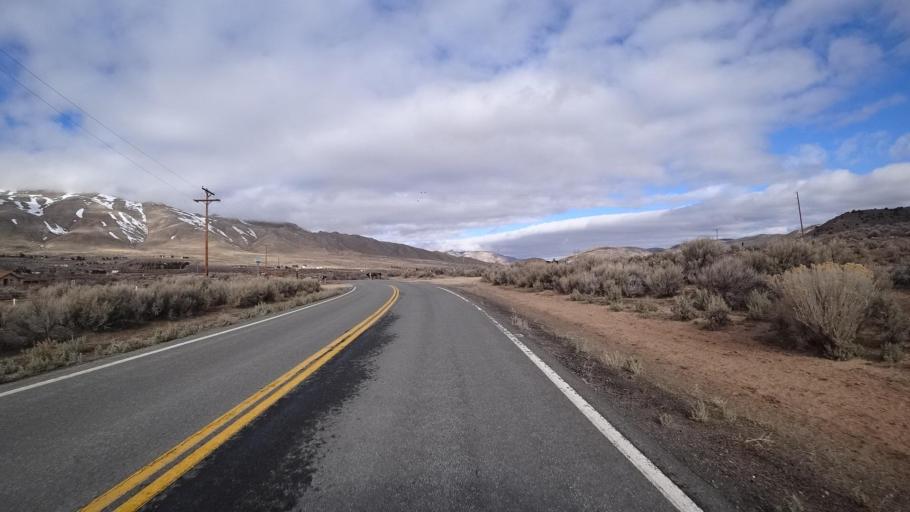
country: US
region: Nevada
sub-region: Washoe County
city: Cold Springs
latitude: 39.8692
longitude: -119.9525
